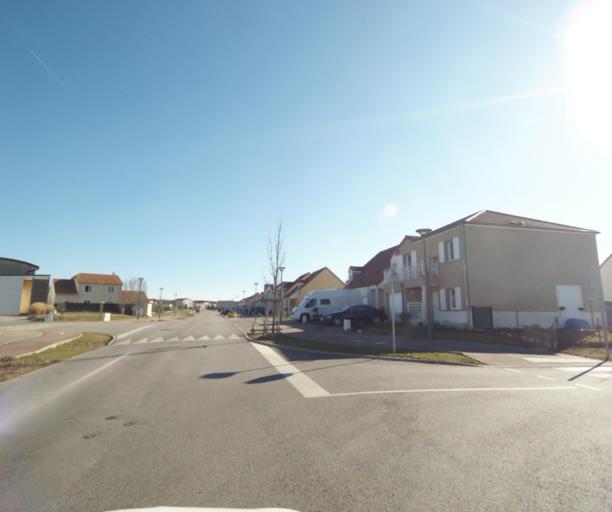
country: FR
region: Lorraine
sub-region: Departement de Meurthe-et-Moselle
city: Tomblaine
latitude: 48.6777
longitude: 6.2282
